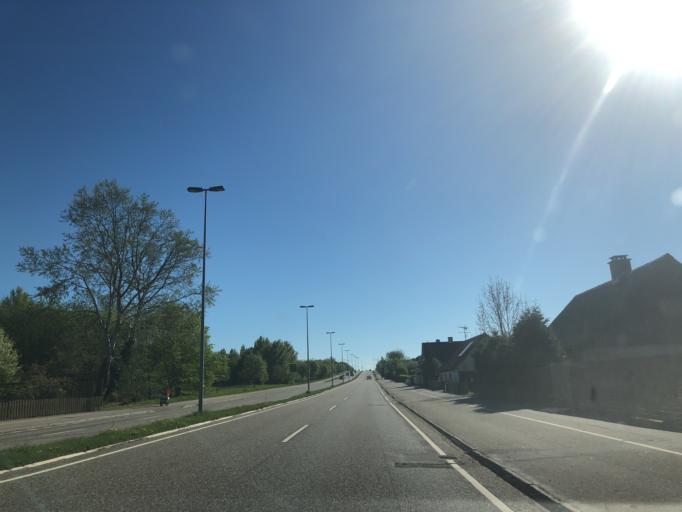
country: DK
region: Zealand
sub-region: Koge Kommune
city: Koge
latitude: 55.4349
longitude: 12.1601
